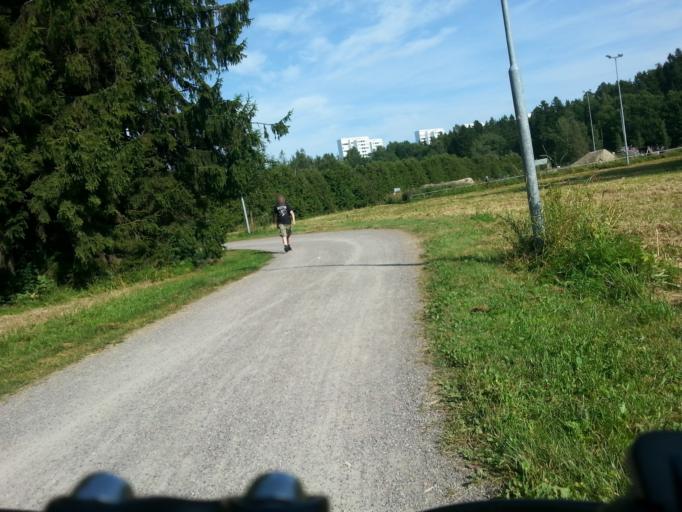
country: FI
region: Uusimaa
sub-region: Helsinki
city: Vantaa
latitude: 60.2362
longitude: 24.9932
